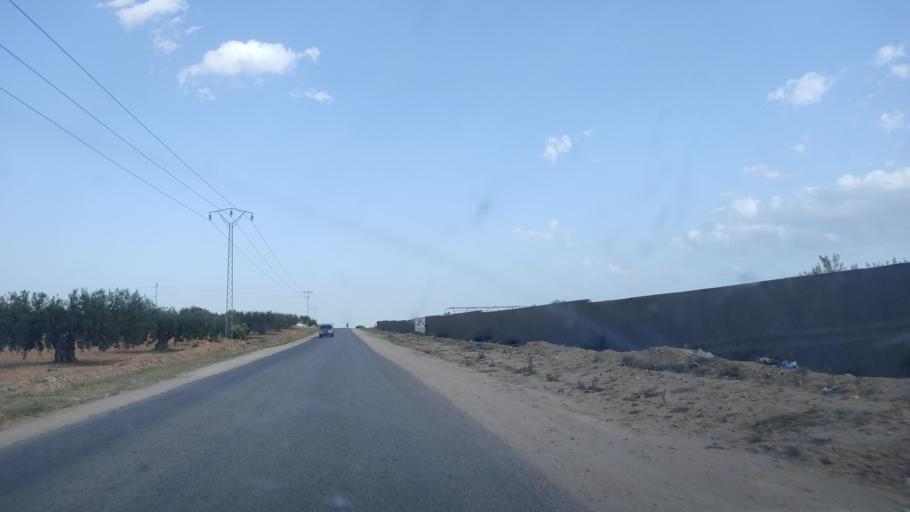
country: TN
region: Safaqis
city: Sfax
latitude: 34.8416
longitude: 10.6227
